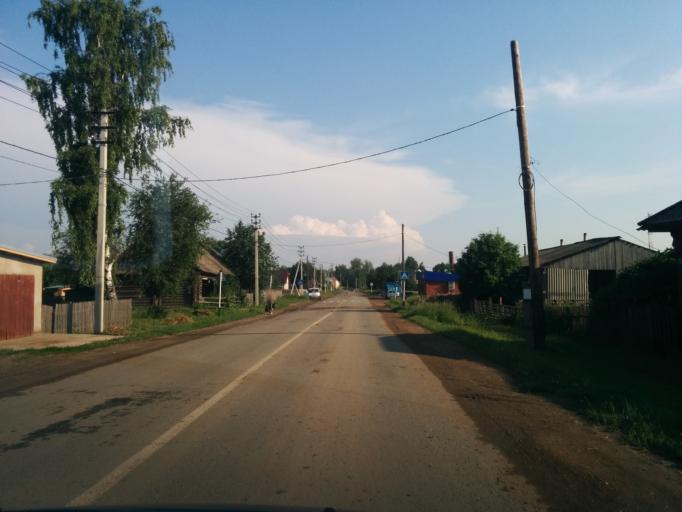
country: RU
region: Perm
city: Polazna
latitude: 58.2356
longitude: 56.2872
